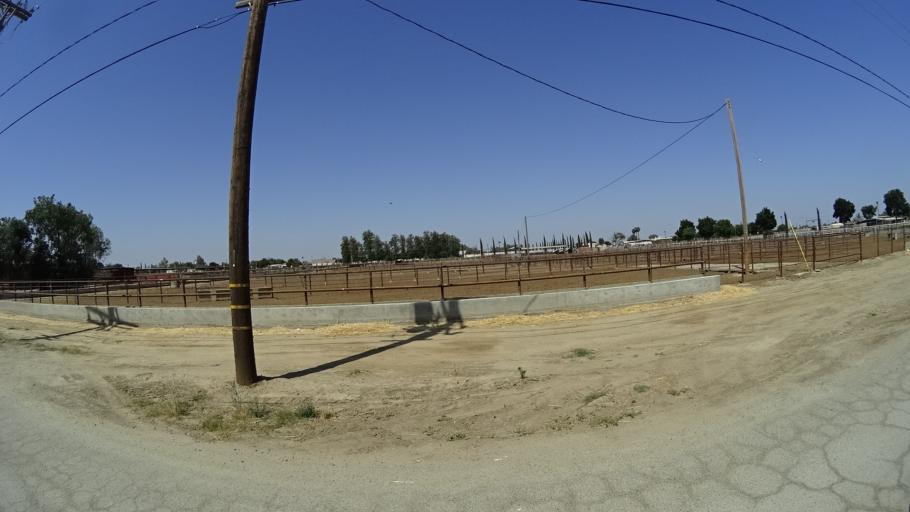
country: US
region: California
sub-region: Kings County
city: Home Garden
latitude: 36.3223
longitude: -119.6167
